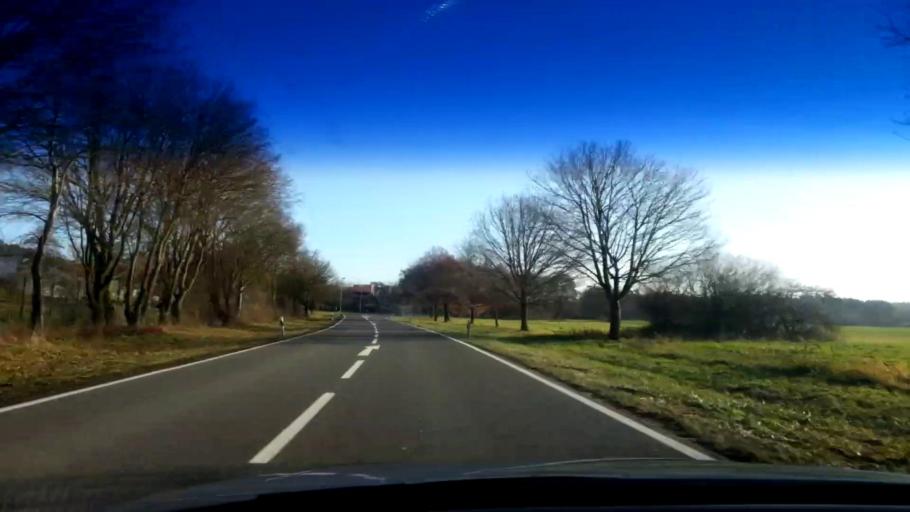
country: DE
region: Bavaria
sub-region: Upper Franconia
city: Memmelsdorf
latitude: 49.9277
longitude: 10.9539
